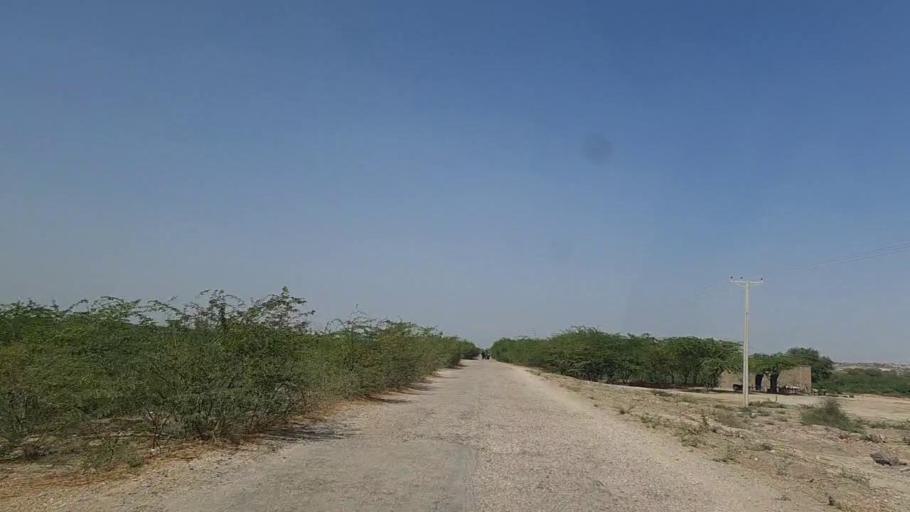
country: PK
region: Sindh
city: Naukot
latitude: 24.6465
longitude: 69.2879
